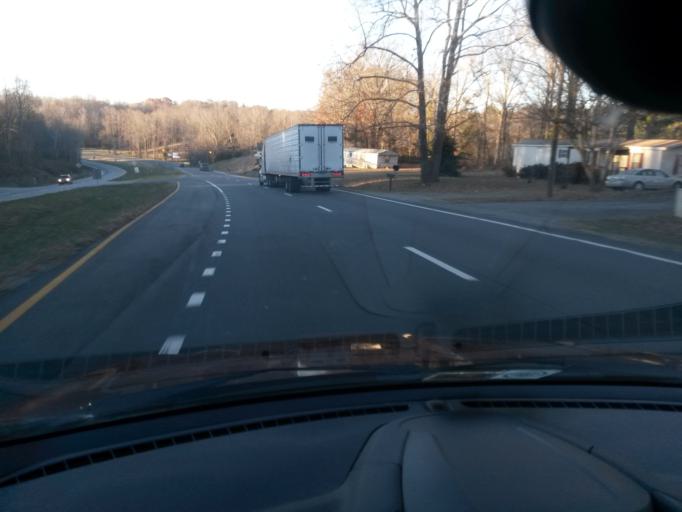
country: US
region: Virginia
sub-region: Franklin County
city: Henry Fork
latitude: 36.8827
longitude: -79.8690
